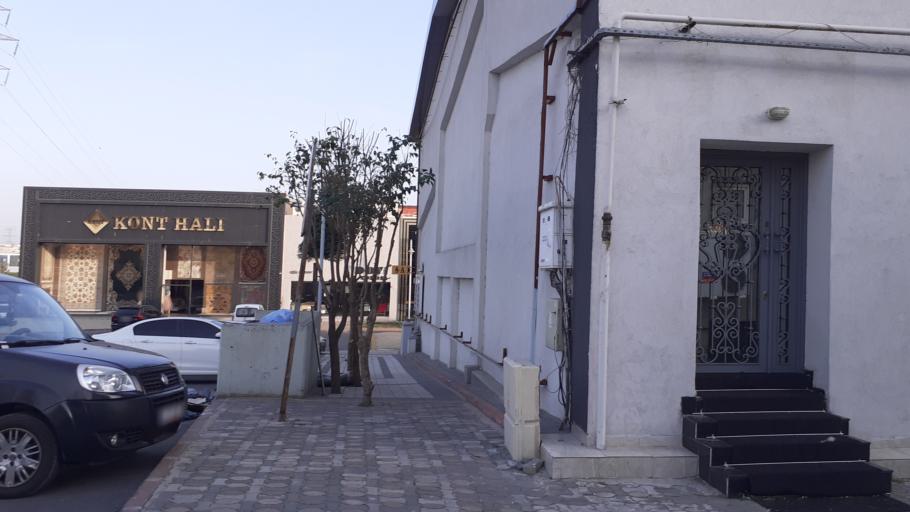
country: TR
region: Istanbul
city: Basaksehir
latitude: 41.0668
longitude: 28.7925
